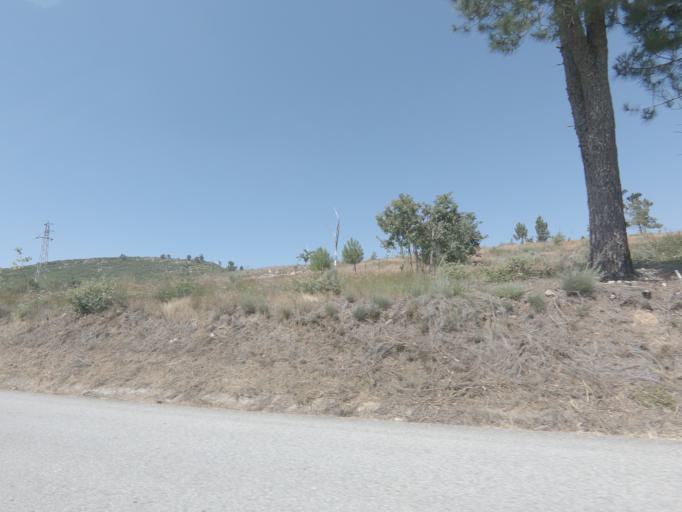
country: PT
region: Viseu
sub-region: Tarouca
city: Tarouca
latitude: 40.9855
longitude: -7.7978
